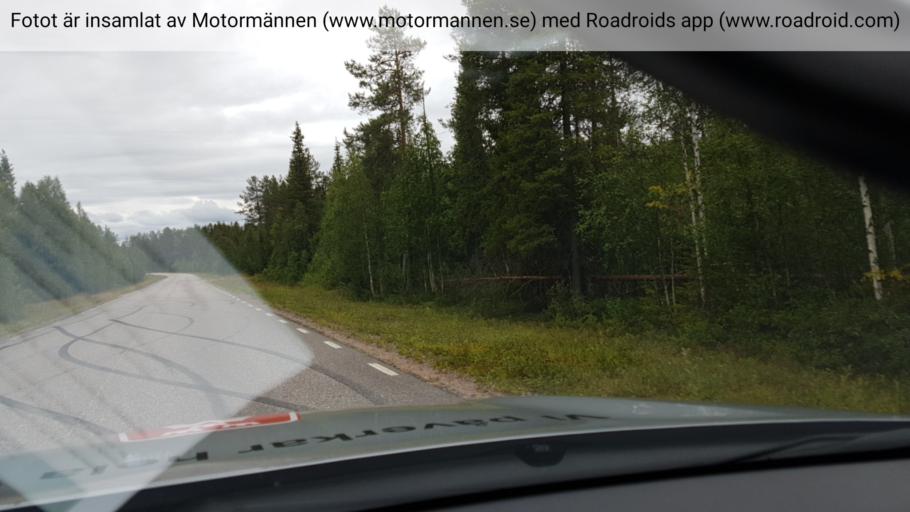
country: SE
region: Norrbotten
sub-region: Pajala Kommun
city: Pajala
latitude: 66.8804
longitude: 23.0397
